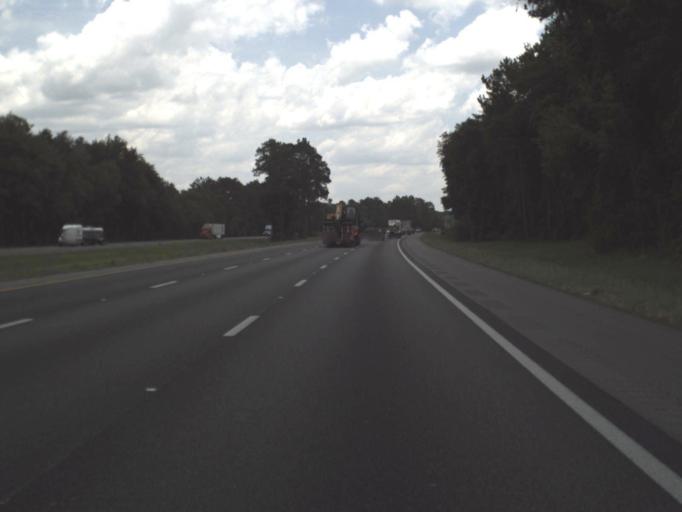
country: US
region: Georgia
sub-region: Echols County
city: Statenville
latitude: 30.6098
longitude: -83.1376
